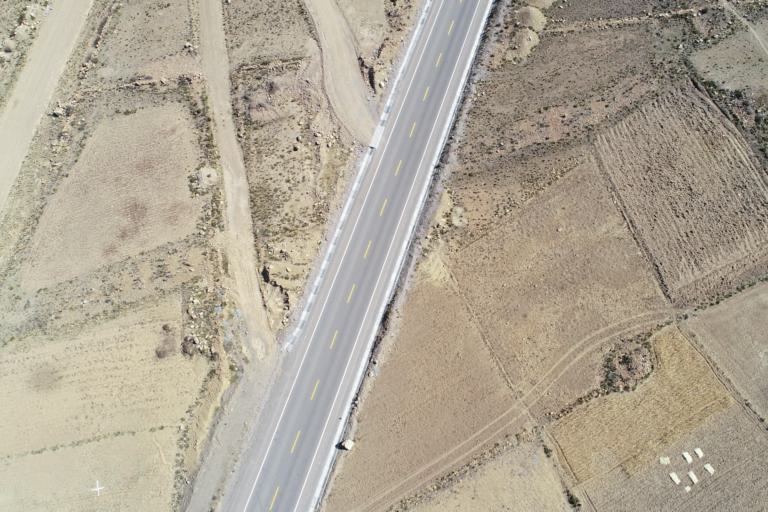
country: BO
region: La Paz
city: Achacachi
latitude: -15.8866
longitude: -68.8103
